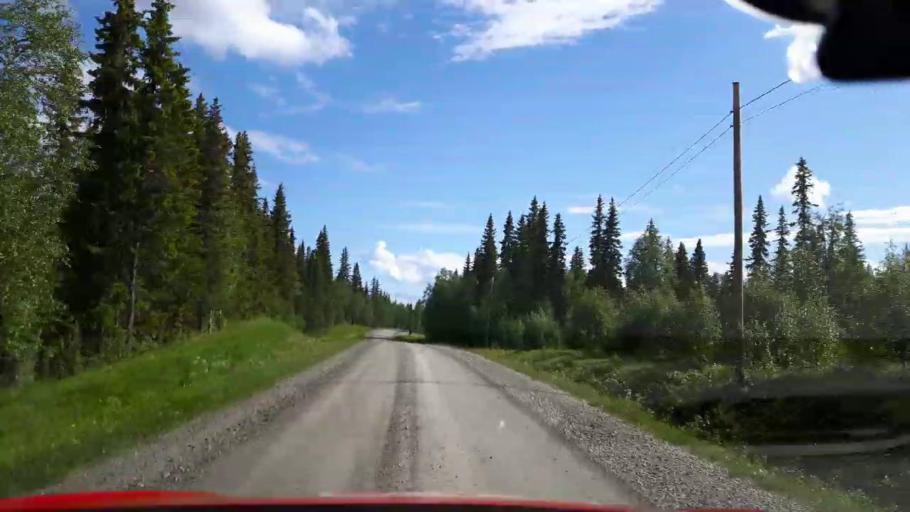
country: SE
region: Jaemtland
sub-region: Krokoms Kommun
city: Valla
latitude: 63.8056
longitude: 14.0493
